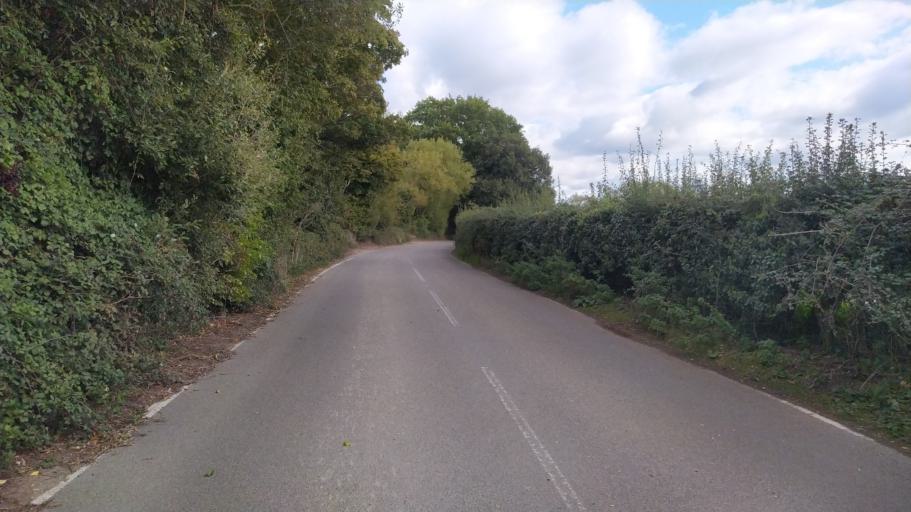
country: GB
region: England
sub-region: West Berkshire
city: Calcot
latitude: 51.4252
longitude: -1.0190
